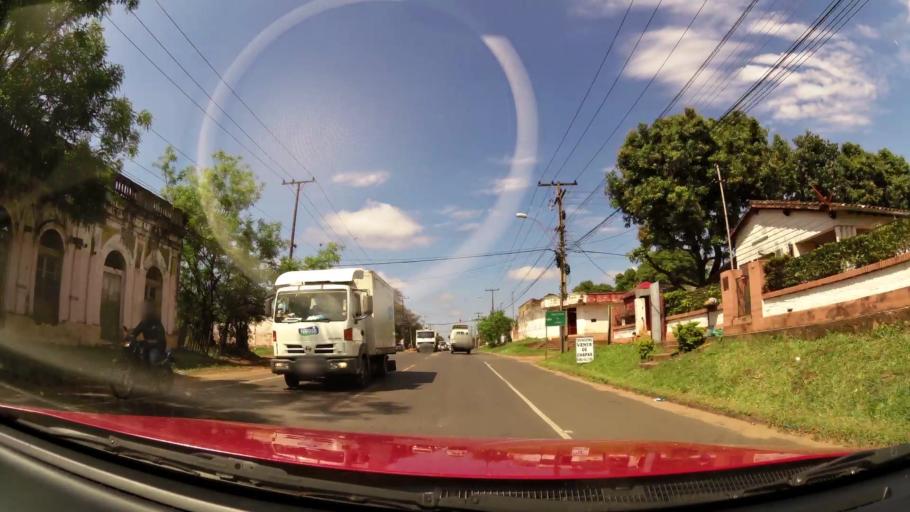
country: PY
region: Central
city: San Lorenzo
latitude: -25.2762
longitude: -57.4970
